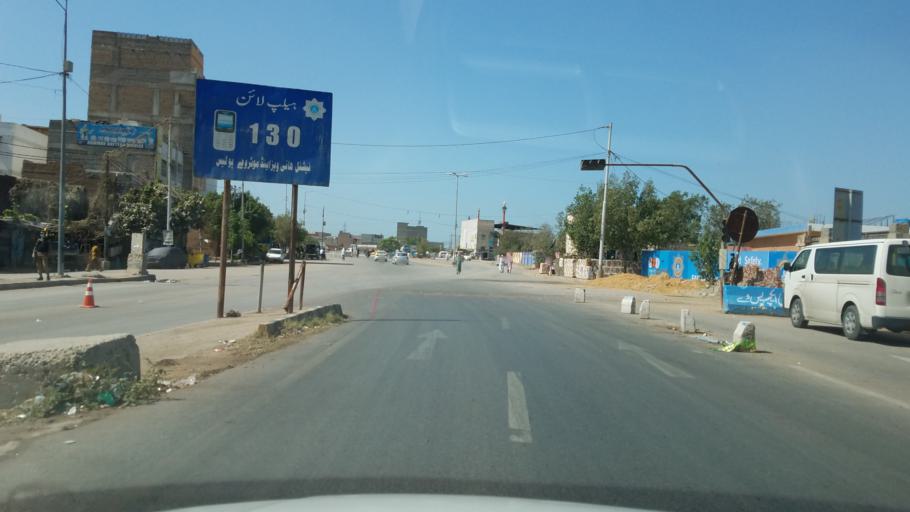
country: PK
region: Sindh
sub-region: Karachi District
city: Karachi
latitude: 24.8719
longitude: 66.9780
